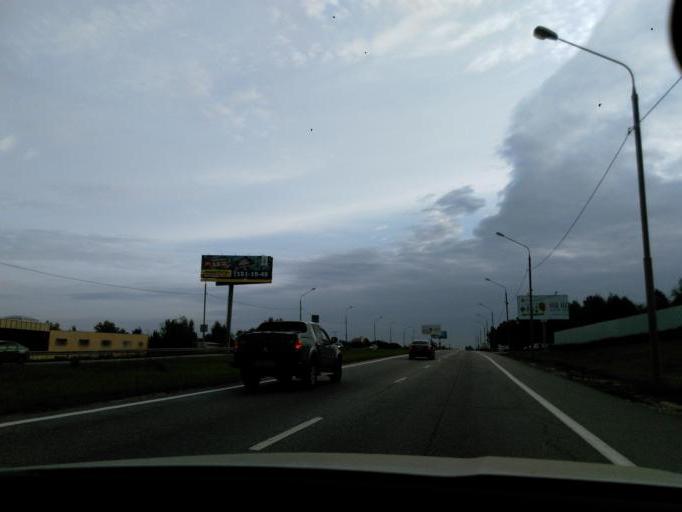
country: RU
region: Moskovskaya
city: Novopodrezkovo
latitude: 55.9740
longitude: 37.3808
